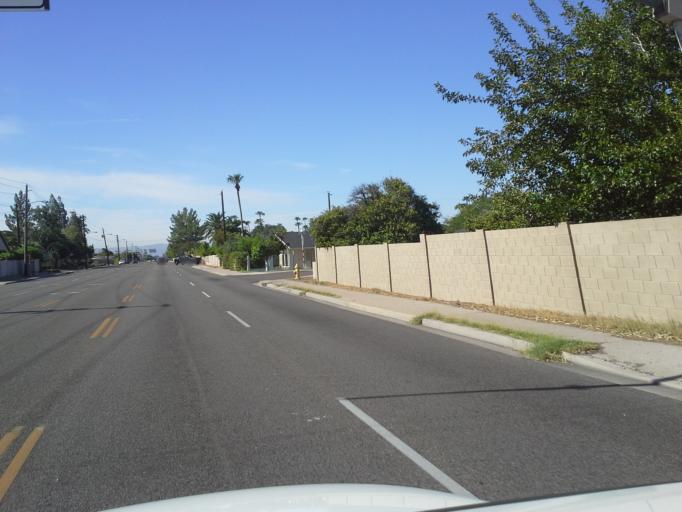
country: US
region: Arizona
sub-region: Maricopa County
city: Phoenix
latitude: 33.5469
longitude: -112.0652
